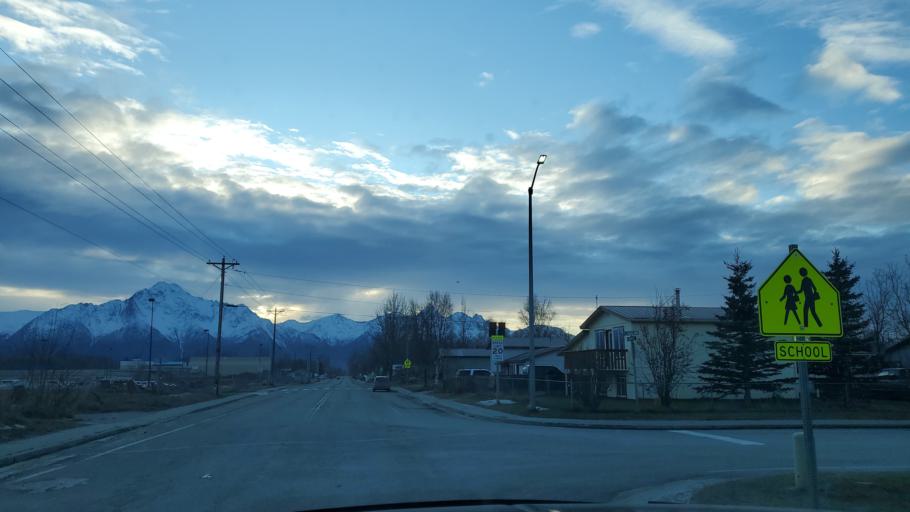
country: US
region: Alaska
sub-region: Matanuska-Susitna Borough
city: Palmer
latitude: 61.6140
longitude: -149.1032
